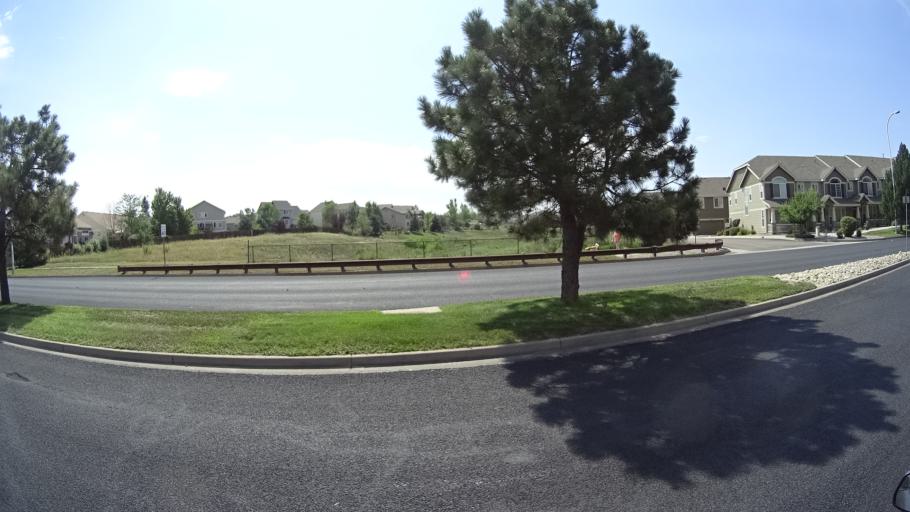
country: US
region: Colorado
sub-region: El Paso County
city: Cimarron Hills
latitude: 38.9274
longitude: -104.7505
